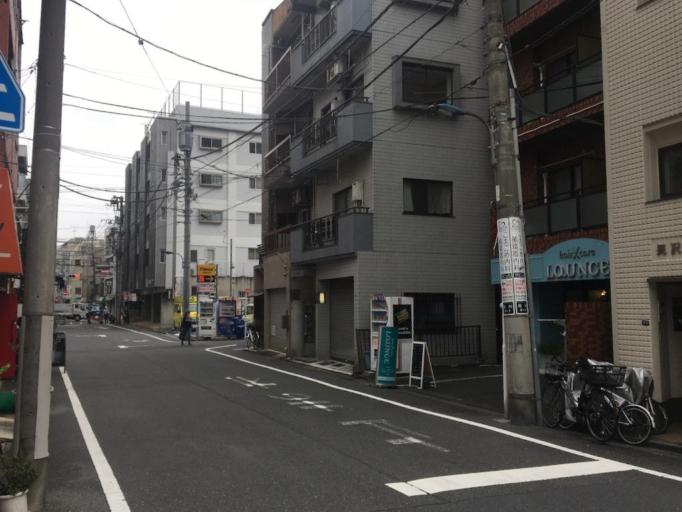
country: JP
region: Tokyo
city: Tokyo
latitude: 35.7359
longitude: 139.7511
